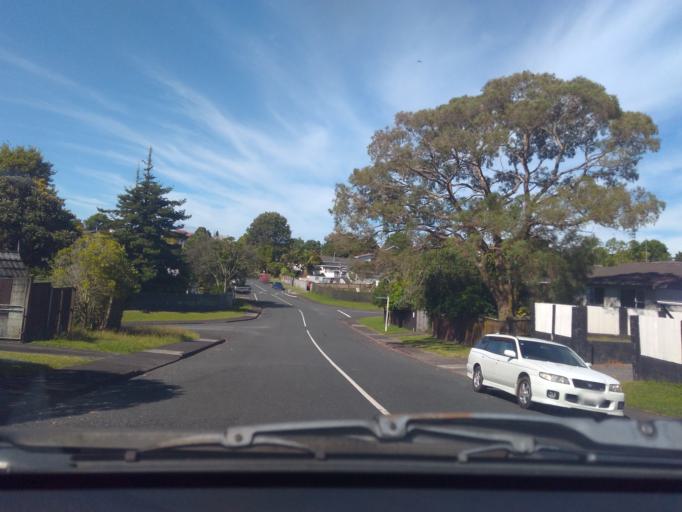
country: NZ
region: Auckland
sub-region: Auckland
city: Waitakere
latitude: -36.8959
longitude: 174.6417
